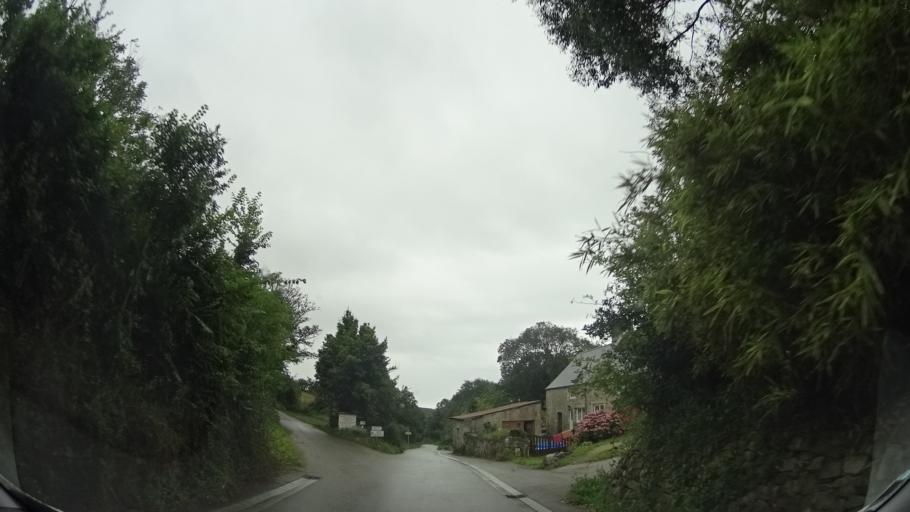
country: FR
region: Lower Normandy
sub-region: Departement de la Manche
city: Beaumont-Hague
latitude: 49.6108
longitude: -1.8228
